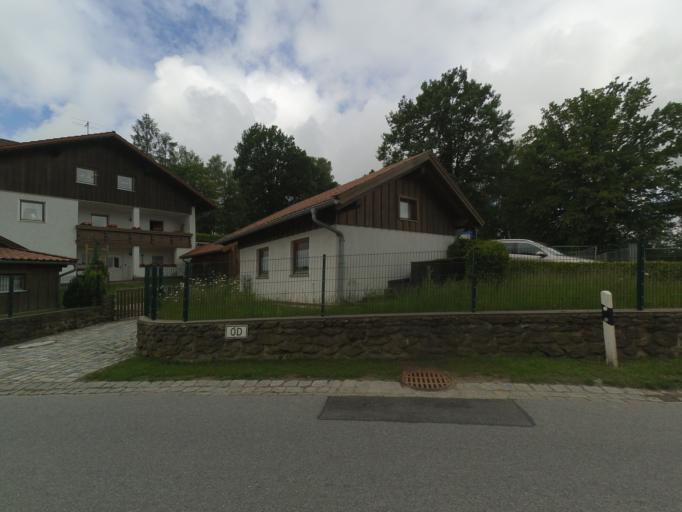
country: DE
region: Bavaria
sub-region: Lower Bavaria
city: Konzell
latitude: 49.0738
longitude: 12.7136
